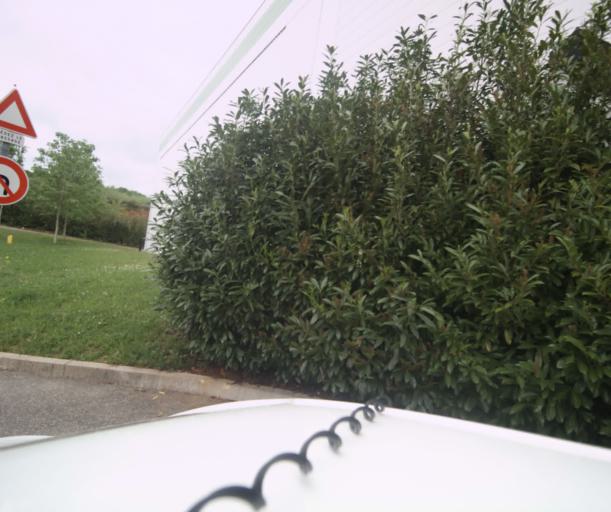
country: FR
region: Franche-Comte
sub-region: Departement du Doubs
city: Franois
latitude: 47.2146
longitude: 5.9440
